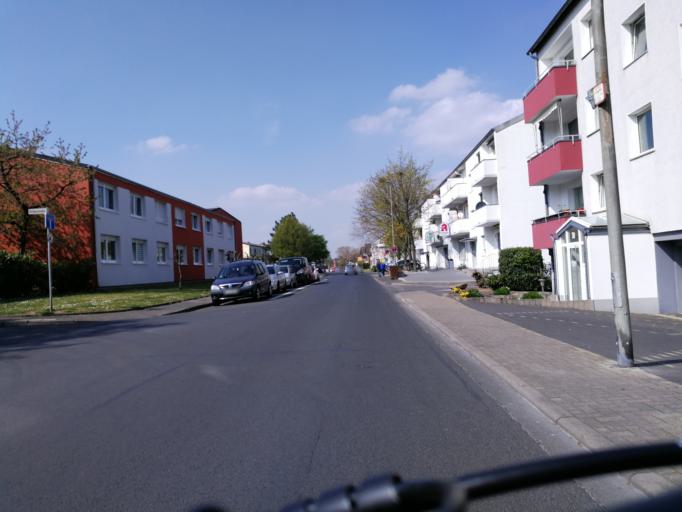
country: DE
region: North Rhine-Westphalia
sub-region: Regierungsbezirk Dusseldorf
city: Dormagen
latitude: 51.1221
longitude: 6.8428
